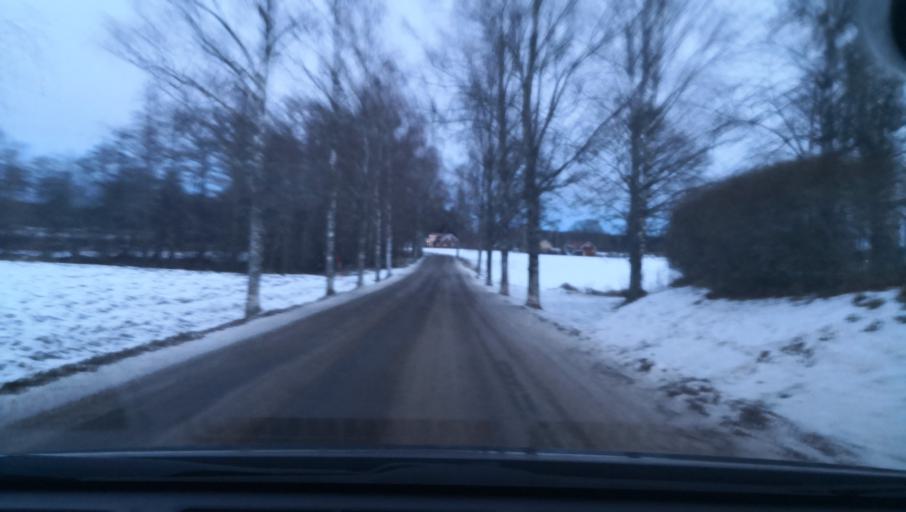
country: SE
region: Dalarna
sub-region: Avesta Kommun
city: Horndal
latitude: 60.2002
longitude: 16.4830
